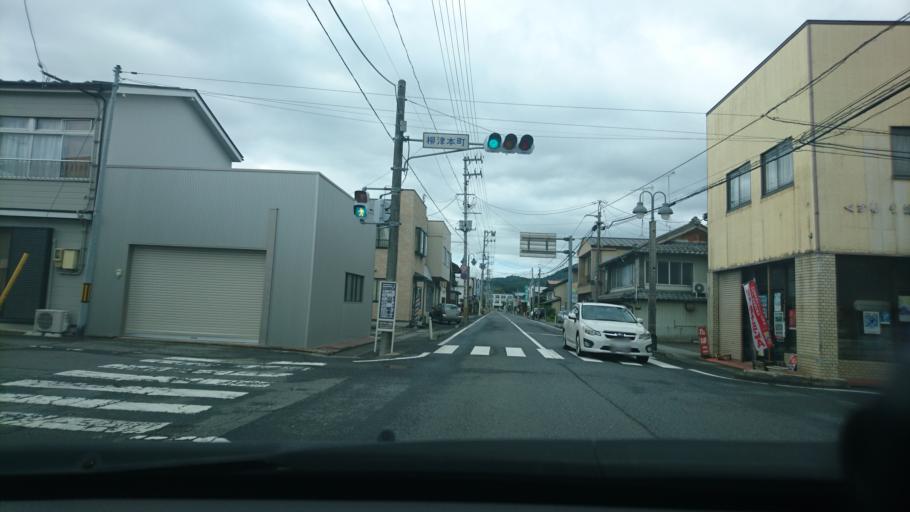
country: JP
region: Miyagi
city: Wakuya
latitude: 38.6126
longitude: 141.3000
